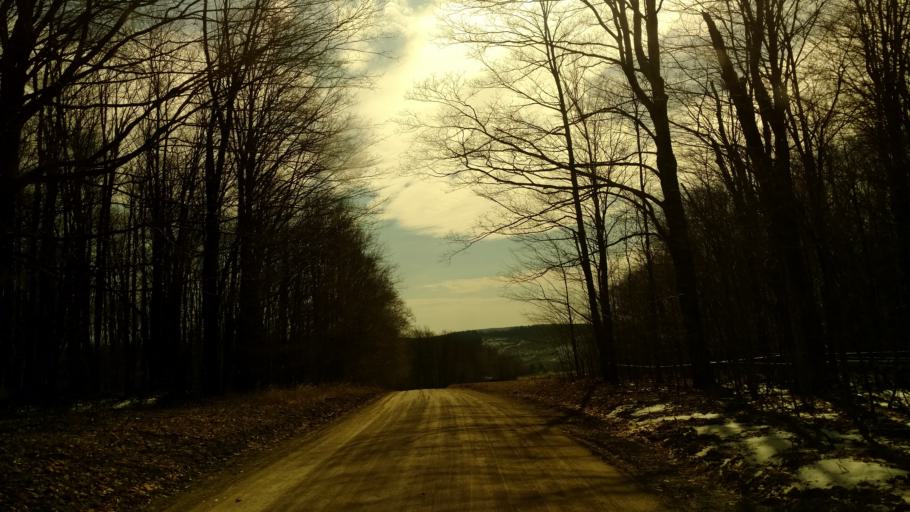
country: US
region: New York
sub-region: Allegany County
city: Andover
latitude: 41.9373
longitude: -77.7690
